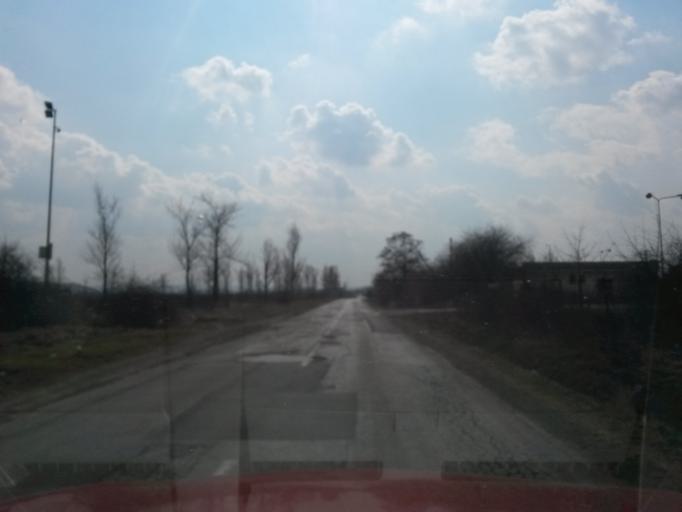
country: SK
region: Kosicky
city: Kosice
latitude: 48.6067
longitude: 21.1739
